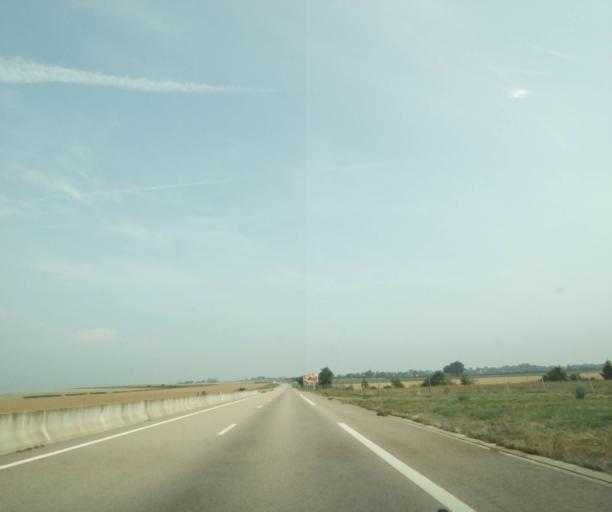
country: FR
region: Lower Normandy
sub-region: Departement de l'Orne
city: Courteilles
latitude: 48.7985
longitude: -0.1263
